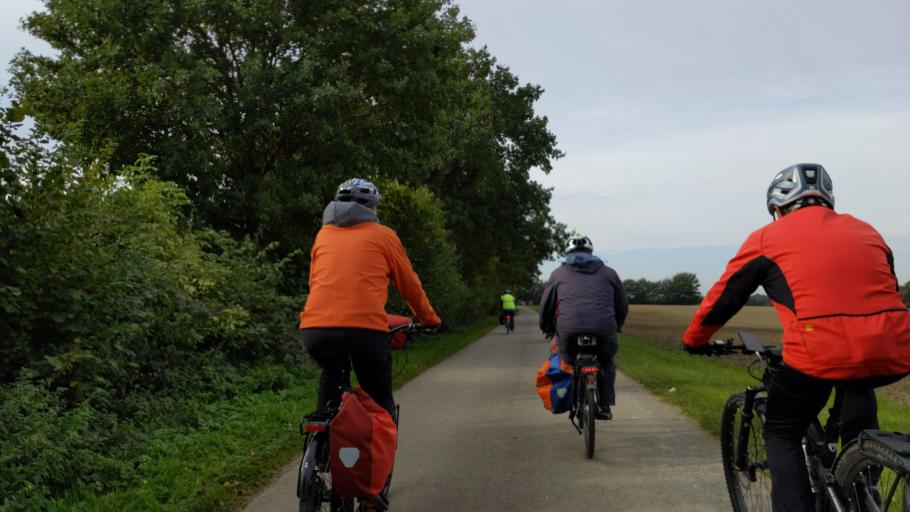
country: DE
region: Schleswig-Holstein
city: Rehhorst
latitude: 53.8826
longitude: 10.4924
